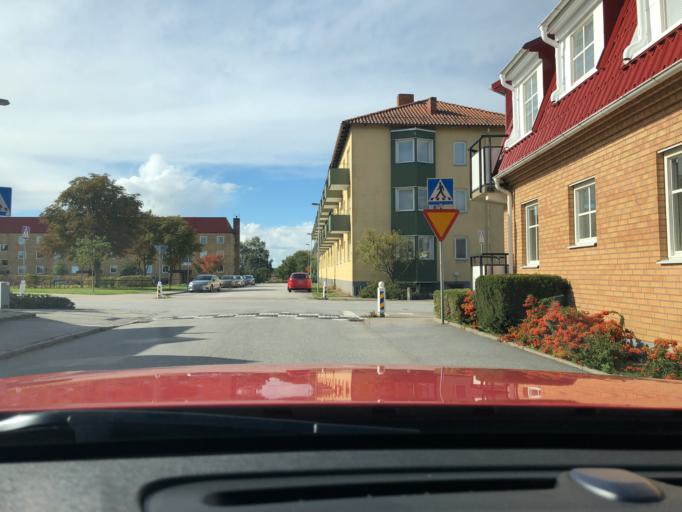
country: SE
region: Skane
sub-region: Sjobo Kommun
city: Sjoebo
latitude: 55.6353
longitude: 13.7044
